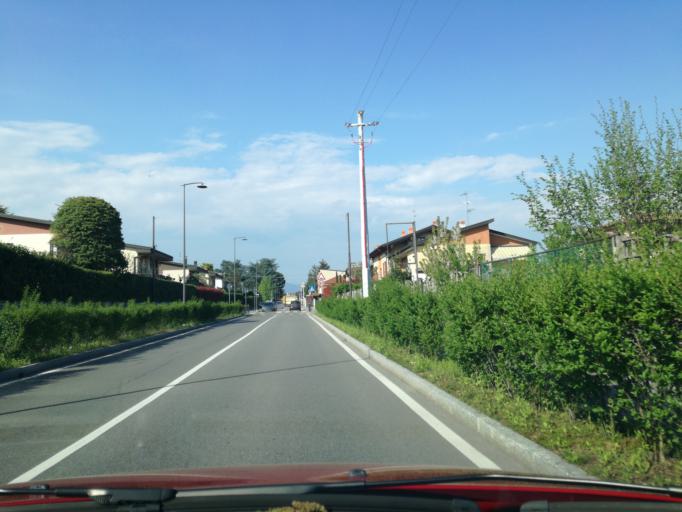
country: IT
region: Lombardy
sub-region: Provincia di Monza e Brianza
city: Cornate d'Adda
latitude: 45.6255
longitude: 9.4673
